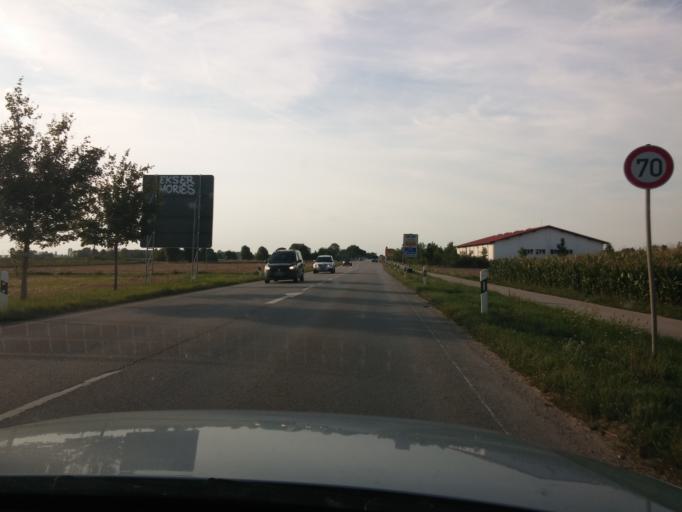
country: DE
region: Bavaria
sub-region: Upper Bavaria
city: Feldkirchen
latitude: 48.1550
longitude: 11.7244
